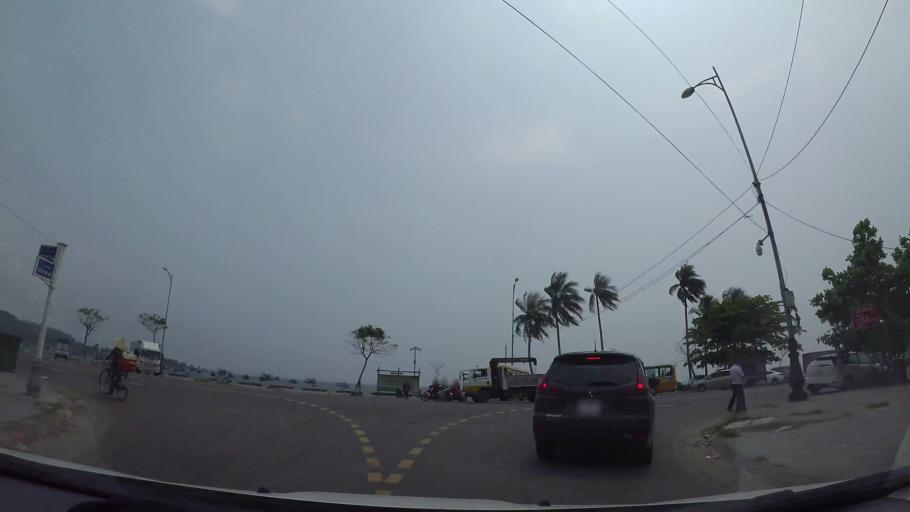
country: VN
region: Da Nang
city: Son Tra
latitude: 16.0996
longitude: 108.2549
